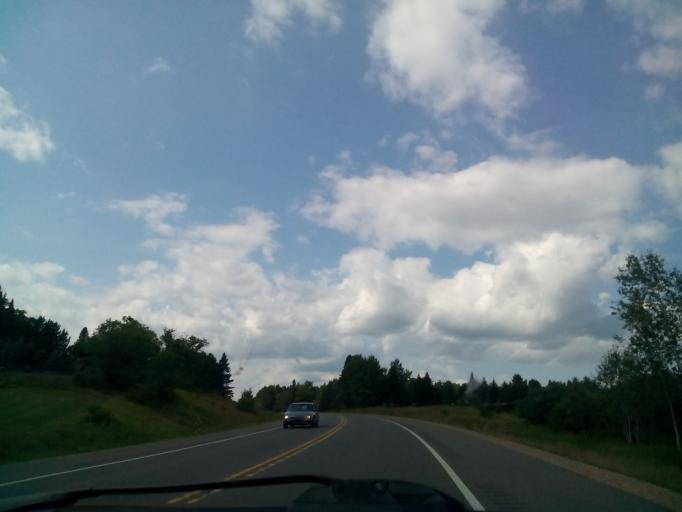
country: US
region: Wisconsin
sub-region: Marinette County
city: Niagara
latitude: 45.5005
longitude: -87.9842
